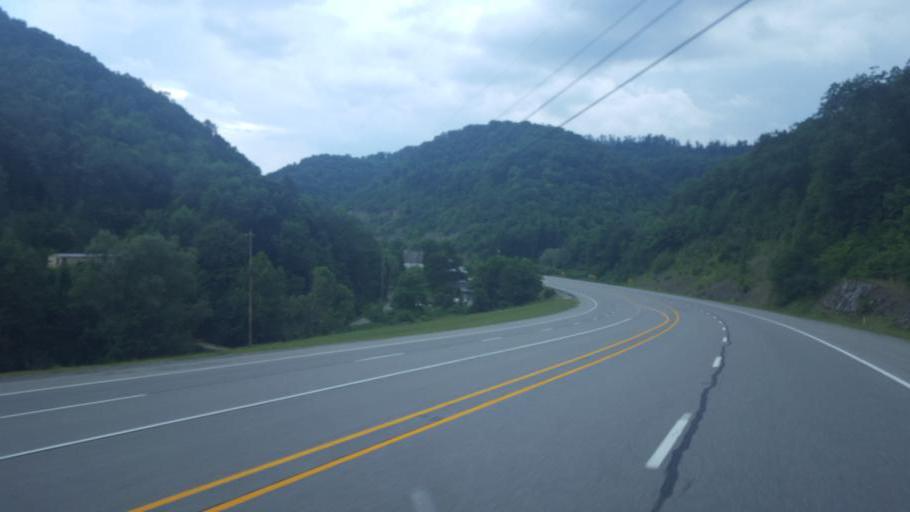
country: US
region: Kentucky
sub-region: Letcher County
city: Jenkins
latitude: 37.2698
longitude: -82.6103
